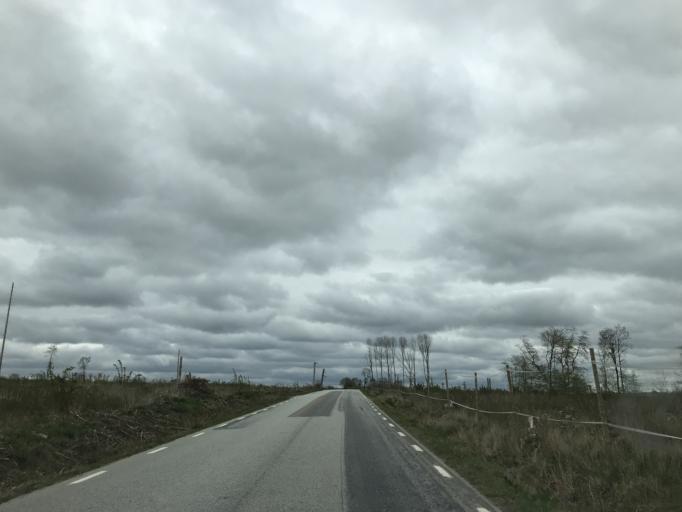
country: SE
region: Skane
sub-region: Eslovs Kommun
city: Eslov
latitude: 55.8872
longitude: 13.2911
